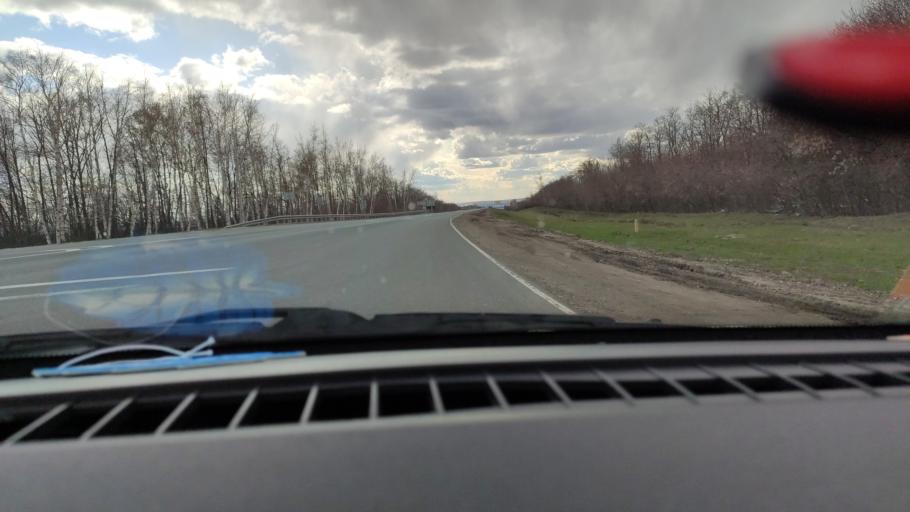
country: RU
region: Saratov
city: Balakovo
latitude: 52.0955
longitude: 47.7218
